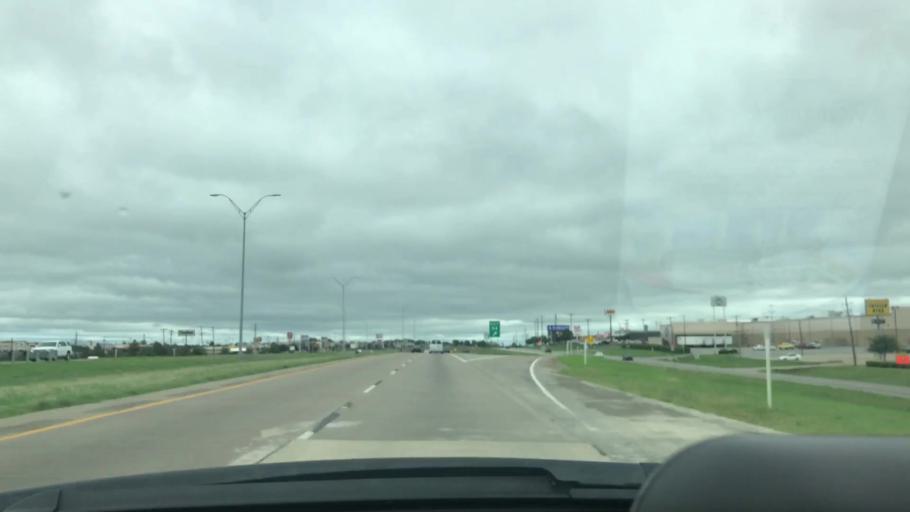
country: US
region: Texas
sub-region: Grayson County
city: Sherman
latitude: 33.6715
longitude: -96.6097
